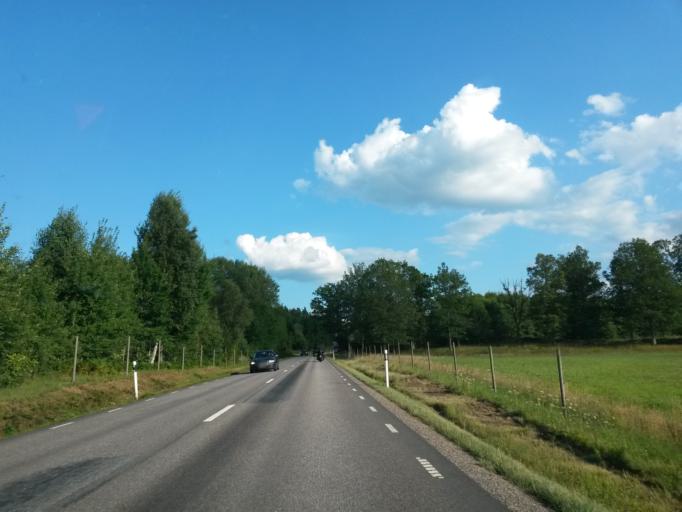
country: SE
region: Vaestra Goetaland
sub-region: Alingsas Kommun
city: Alingsas
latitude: 57.9603
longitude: 12.4481
